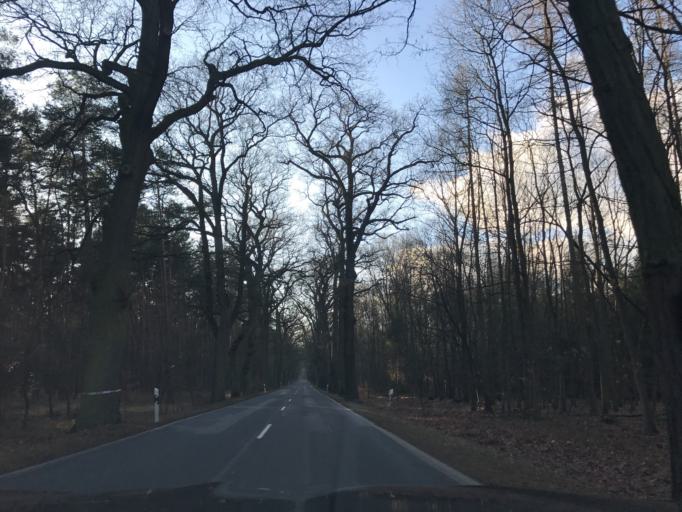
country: DE
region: Saxony-Anhalt
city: Mockern
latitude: 52.1633
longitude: 12.0001
